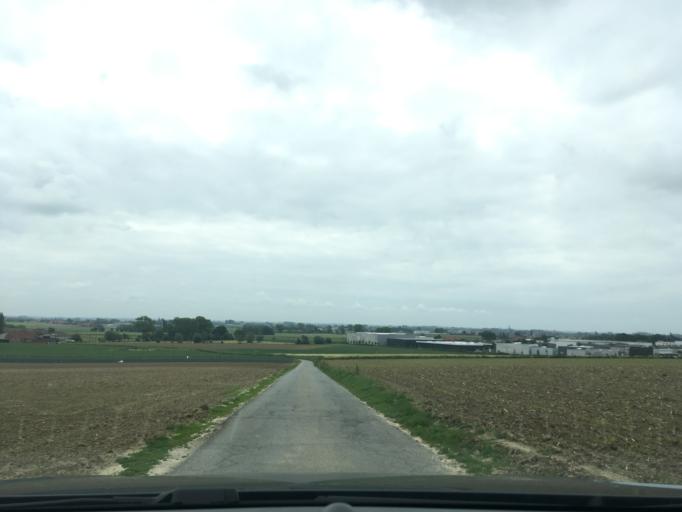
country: BE
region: Flanders
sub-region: Provincie West-Vlaanderen
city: Moorslede
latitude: 50.8948
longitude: 3.0821
